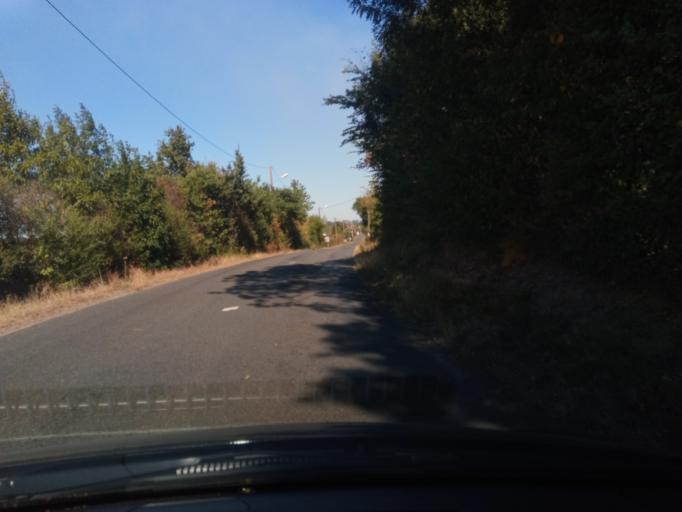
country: FR
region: Poitou-Charentes
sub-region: Departement de la Vienne
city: Montmorillon
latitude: 46.4351
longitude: 0.8787
